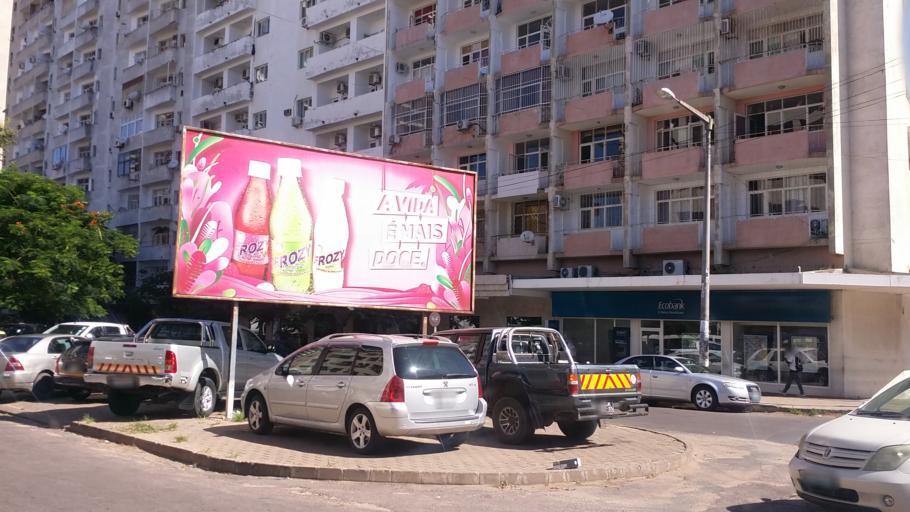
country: MZ
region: Maputo City
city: Maputo
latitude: -25.9758
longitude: 32.5912
